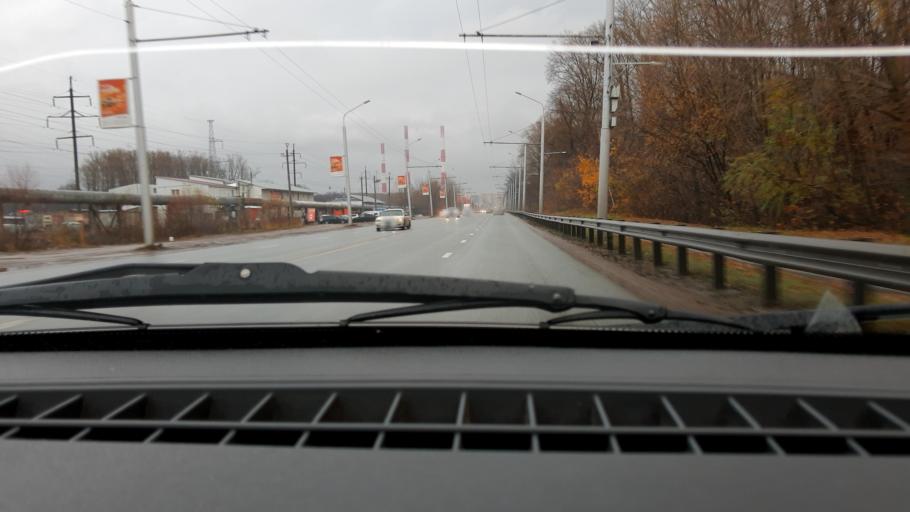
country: RU
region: Bashkortostan
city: Ufa
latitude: 54.7901
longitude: 56.0963
